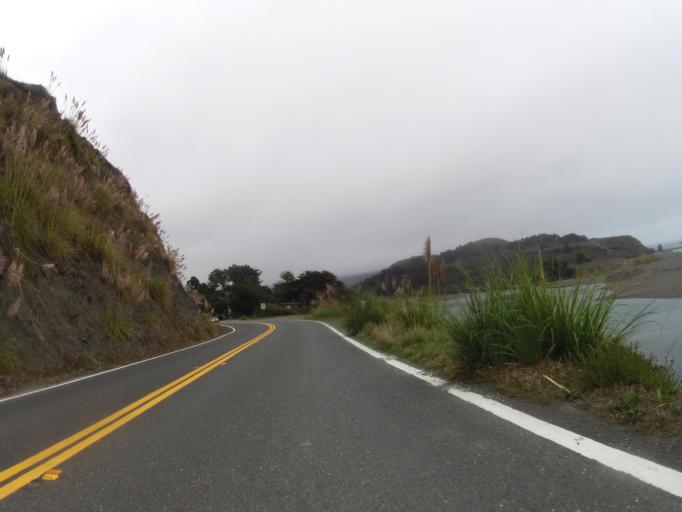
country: US
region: California
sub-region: Sonoma County
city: Monte Rio
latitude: 38.4523
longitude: -123.1278
